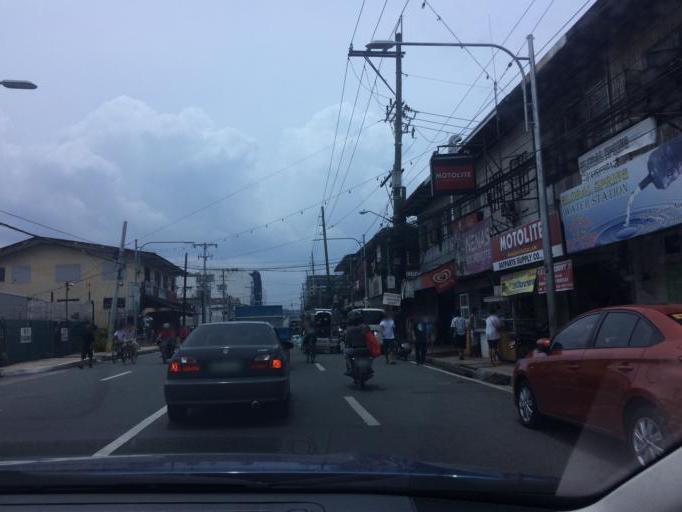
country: PH
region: Metro Manila
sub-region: Makati City
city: Makati City
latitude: 14.5242
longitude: 120.9969
